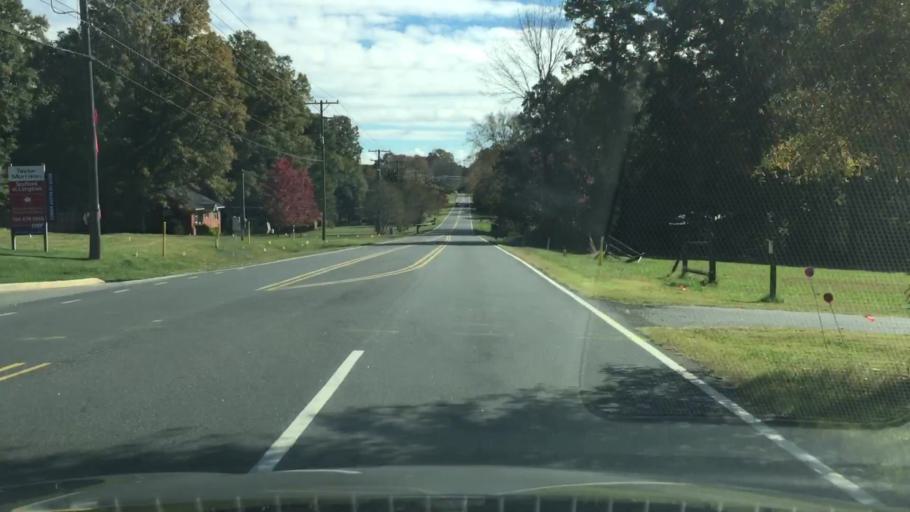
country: US
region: North Carolina
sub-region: Gaston County
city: Davidson
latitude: 35.5412
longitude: -80.8397
